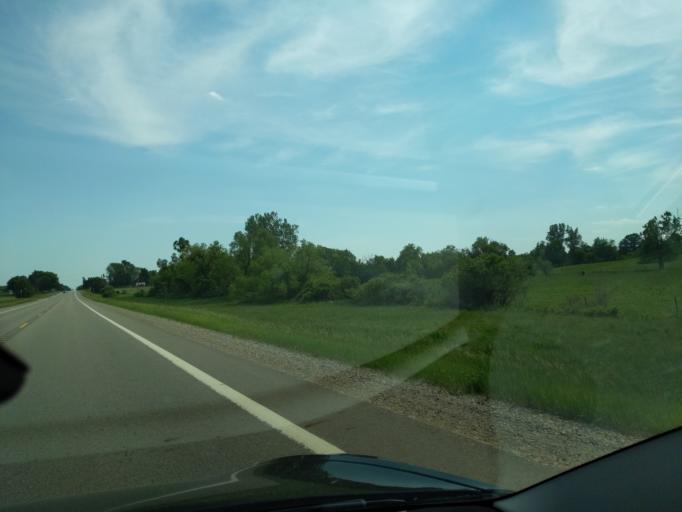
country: US
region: Michigan
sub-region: Barry County
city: Nashville
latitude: 42.6559
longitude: -85.0950
